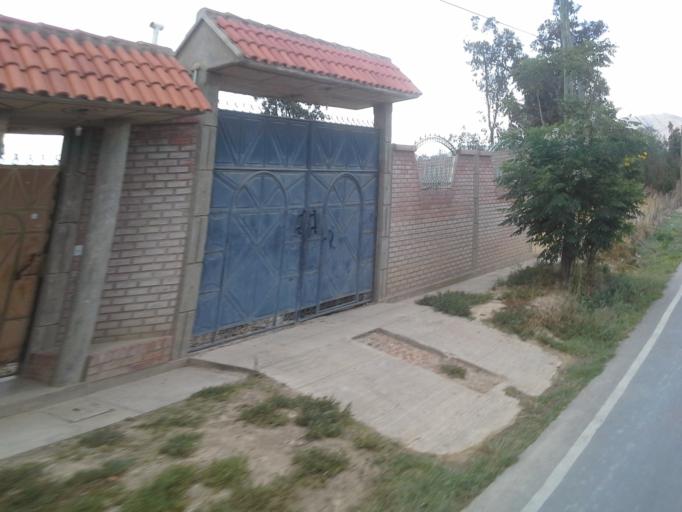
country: BO
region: Cochabamba
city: Tarata
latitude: -17.5824
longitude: -66.0161
